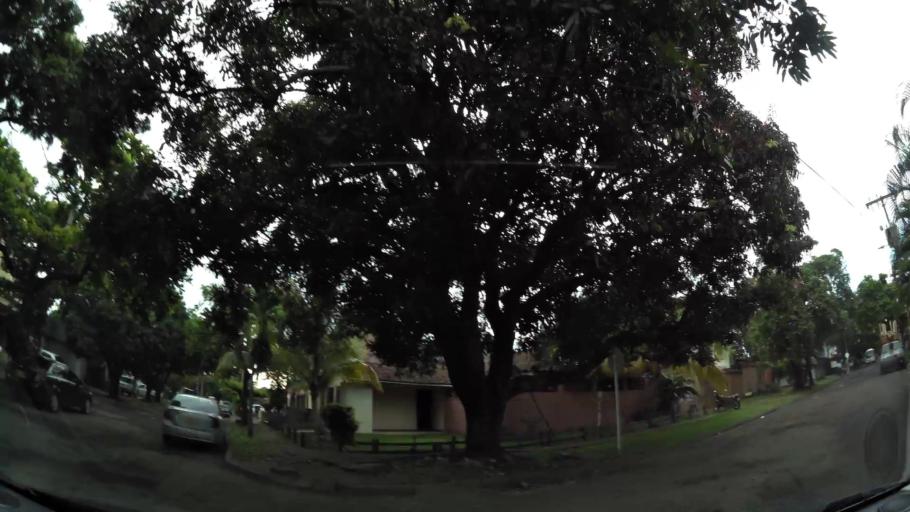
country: CO
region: Valle del Cauca
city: Cali
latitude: 3.4847
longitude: -76.5184
